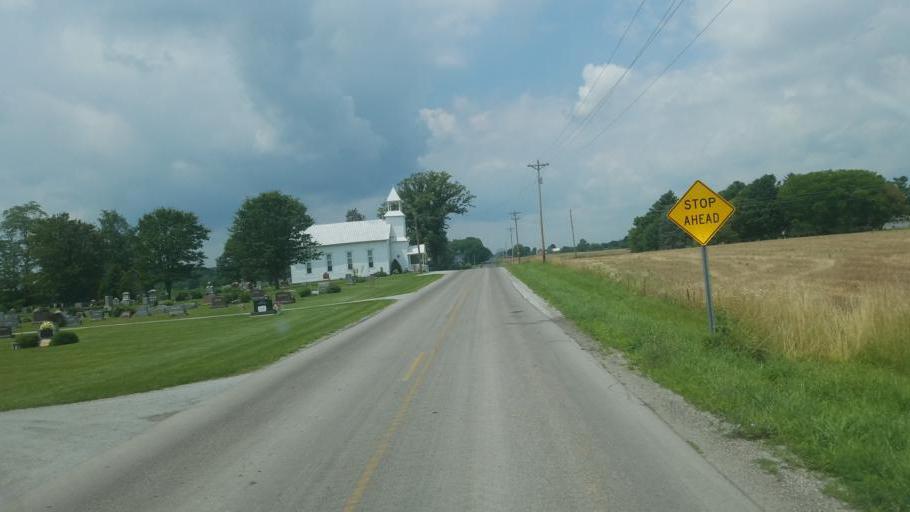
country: US
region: Ohio
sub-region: Hardin County
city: Kenton
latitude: 40.5844
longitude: -83.5032
